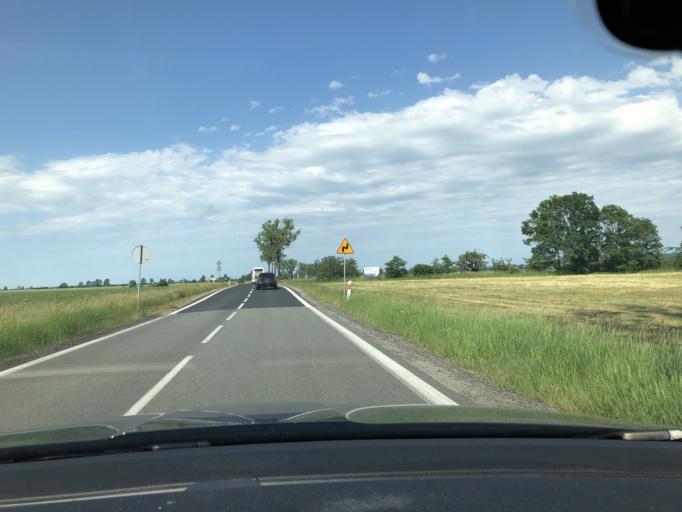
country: PL
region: Lower Silesian Voivodeship
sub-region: Powiat jaworski
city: Paszowice
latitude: 50.9788
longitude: 16.1621
